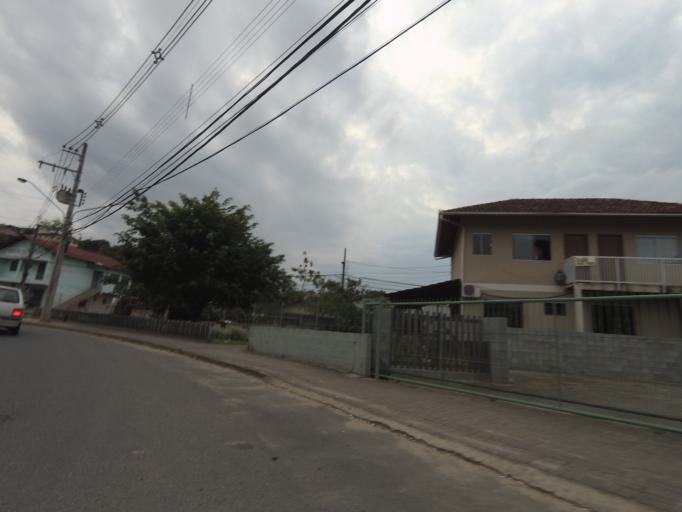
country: BR
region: Santa Catarina
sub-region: Blumenau
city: Blumenau
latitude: -26.8757
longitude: -49.0581
